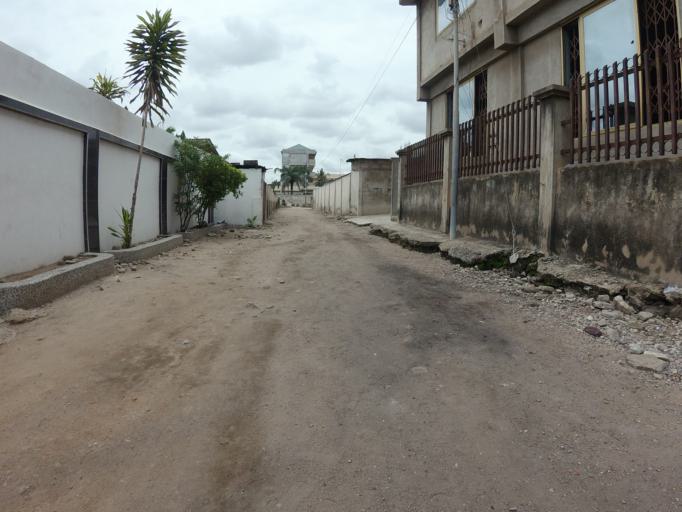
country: GH
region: Greater Accra
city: Accra
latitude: 5.5941
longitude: -0.2174
